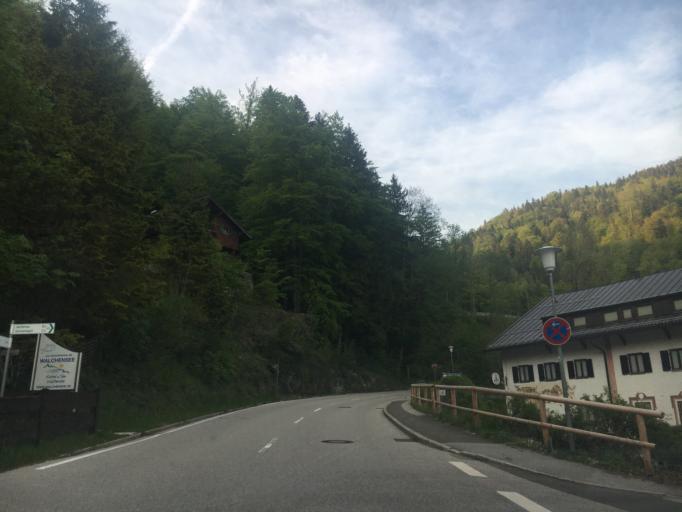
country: DE
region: Bavaria
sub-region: Upper Bavaria
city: Schlehdorf
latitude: 47.6181
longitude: 11.3461
